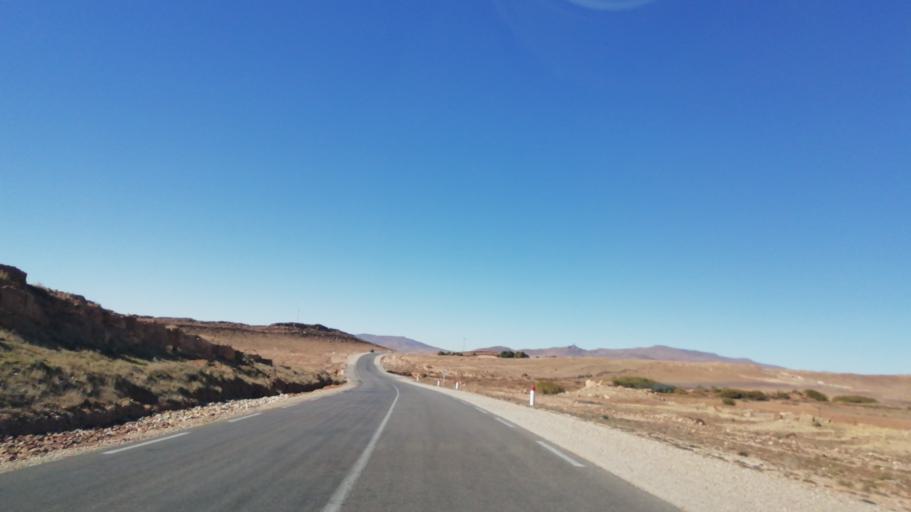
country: DZ
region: El Bayadh
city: El Bayadh
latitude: 33.6092
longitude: 1.2399
